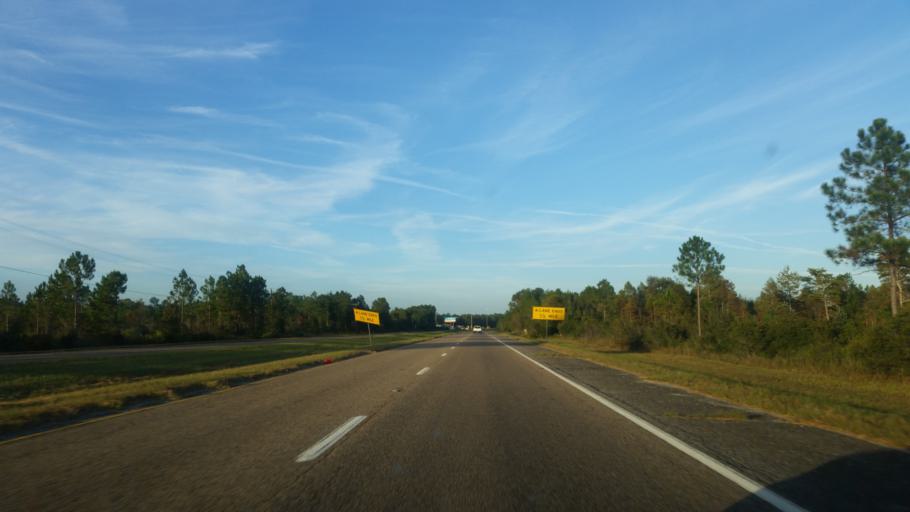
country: US
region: Alabama
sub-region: Mobile County
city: Grand Bay
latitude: 30.4659
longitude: -88.4098
